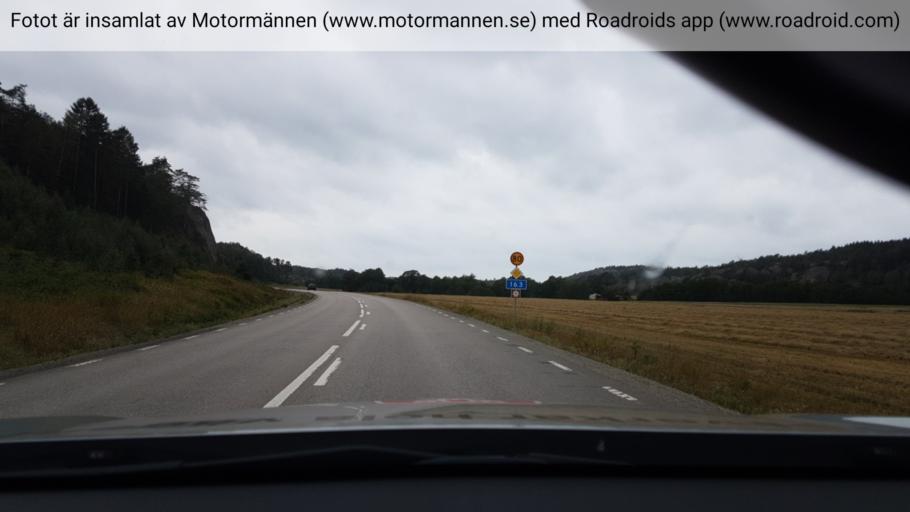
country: SE
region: Vaestra Goetaland
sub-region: Tanums Kommun
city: Tanumshede
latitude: 58.7309
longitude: 11.3073
